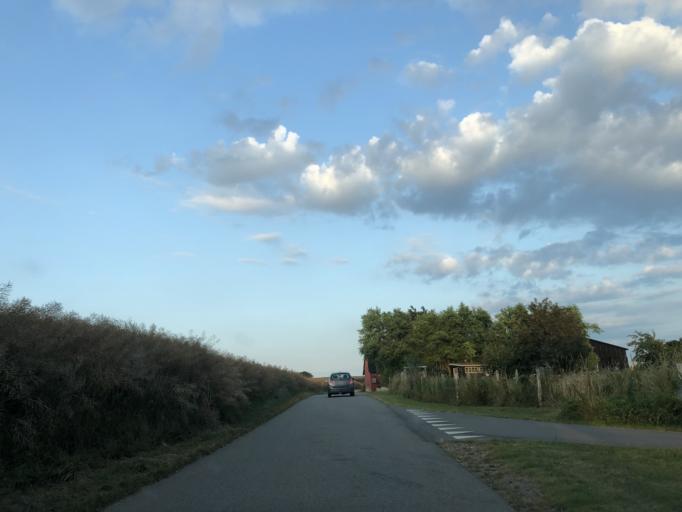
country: DK
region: South Denmark
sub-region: Kerteminde Kommune
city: Munkebo
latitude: 55.5126
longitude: 10.6051
